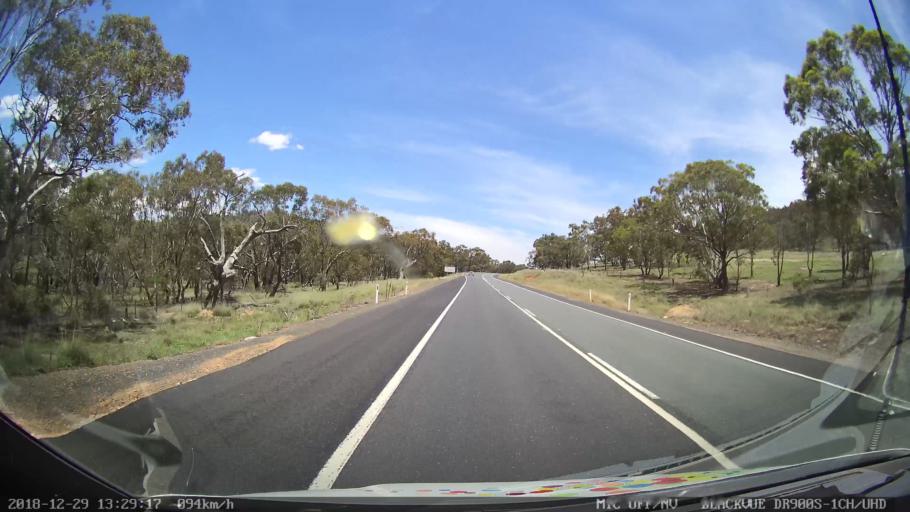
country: AU
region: New South Wales
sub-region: Cooma-Monaro
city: Cooma
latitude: -35.8880
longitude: 149.1616
